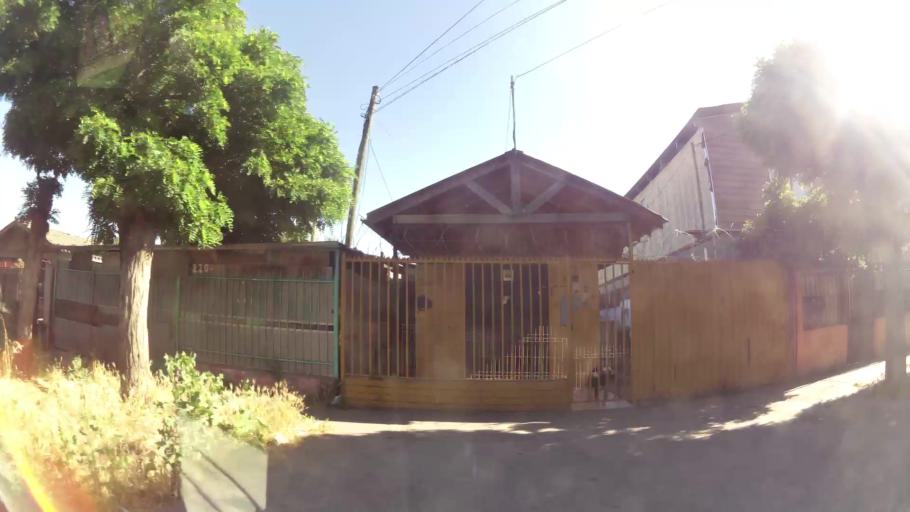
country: CL
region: Santiago Metropolitan
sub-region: Provincia de Maipo
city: San Bernardo
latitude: -33.6172
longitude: -70.6952
